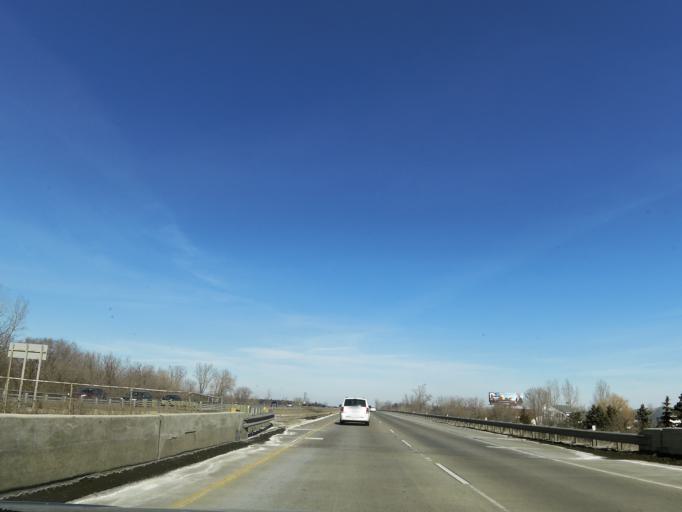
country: US
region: Minnesota
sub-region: Ramsey County
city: North Saint Paul
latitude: 45.0210
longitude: -92.9593
